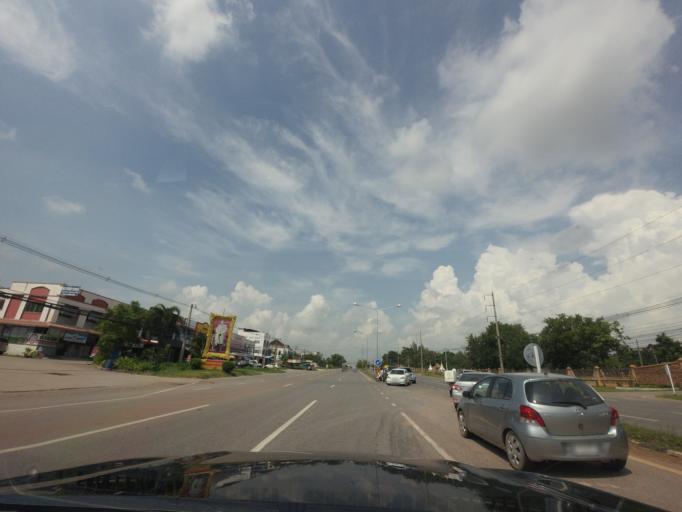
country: TH
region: Khon Kaen
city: Ban Fang
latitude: 16.4503
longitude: 102.7281
